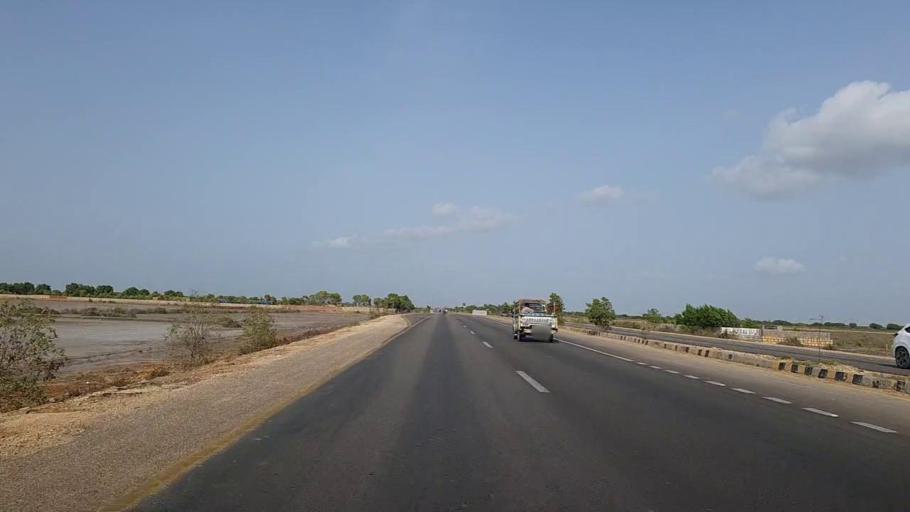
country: PK
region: Sindh
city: Gharo
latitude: 24.7383
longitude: 67.7295
